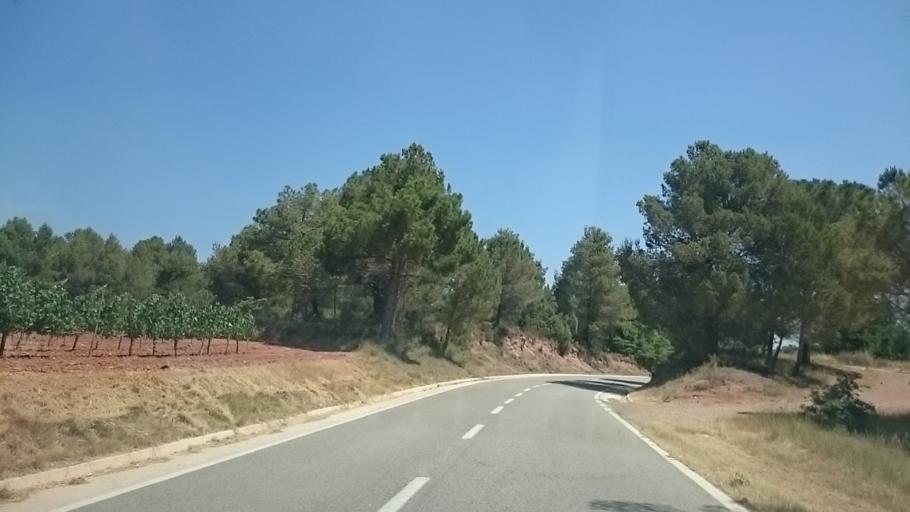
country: ES
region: Catalonia
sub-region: Provincia de Barcelona
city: Sant Marti de Tous
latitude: 41.4844
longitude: 1.5021
